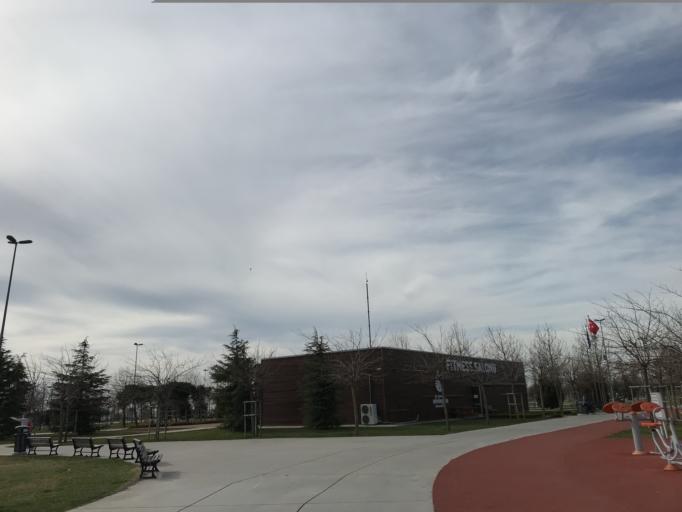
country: TR
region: Istanbul
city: Maltepe
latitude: 40.9344
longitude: 29.1134
